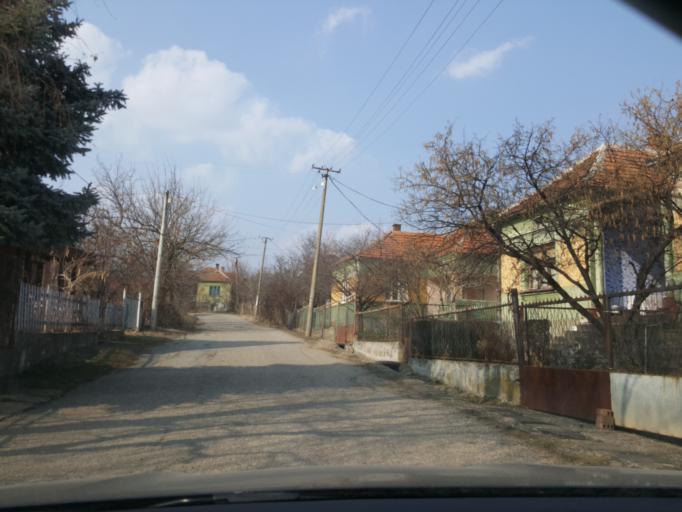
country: RS
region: Central Serbia
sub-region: Nisavski Okrug
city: Aleksinac
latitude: 43.5353
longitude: 21.7421
